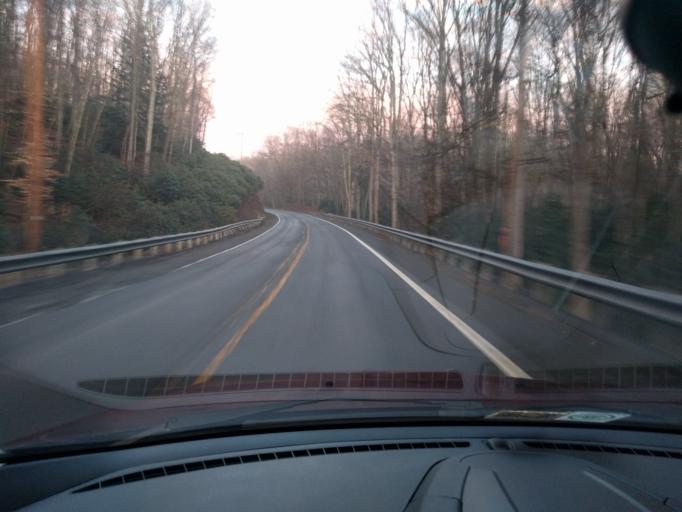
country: US
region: West Virginia
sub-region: Fayette County
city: Fayetteville
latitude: 38.0488
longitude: -80.9426
